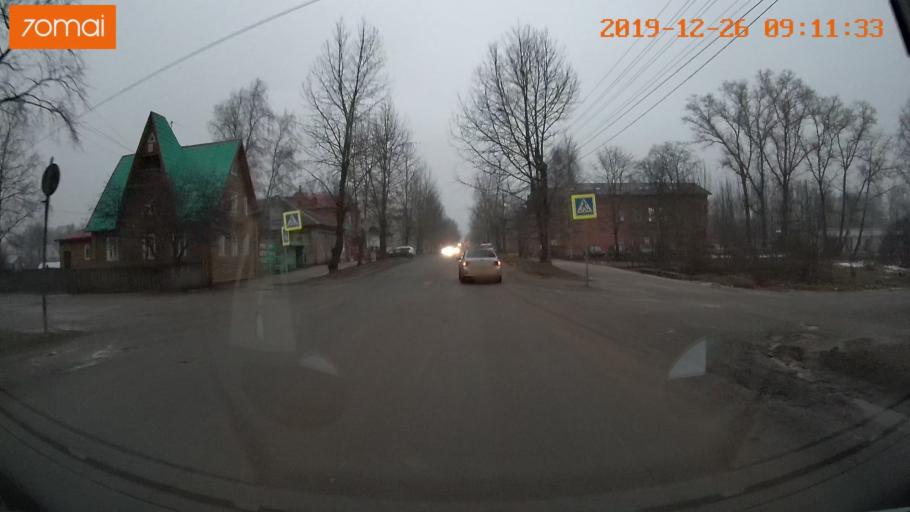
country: RU
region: Vologda
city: Gryazovets
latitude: 58.8768
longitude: 40.2528
